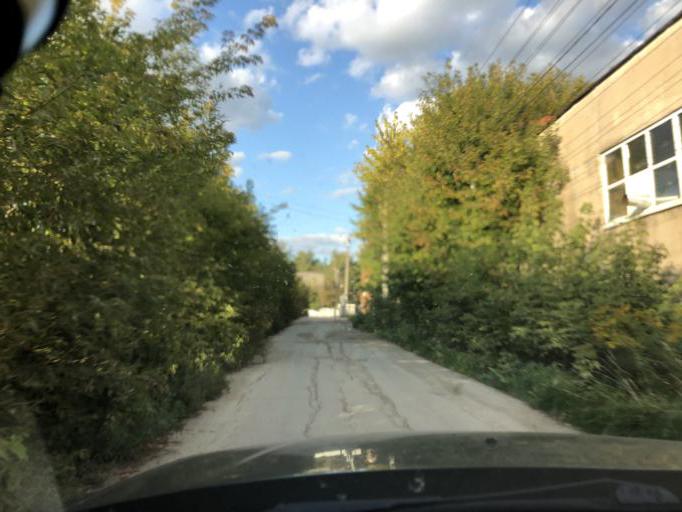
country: RU
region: Tula
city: Mendeleyevskiy
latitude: 54.1847
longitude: 37.5421
